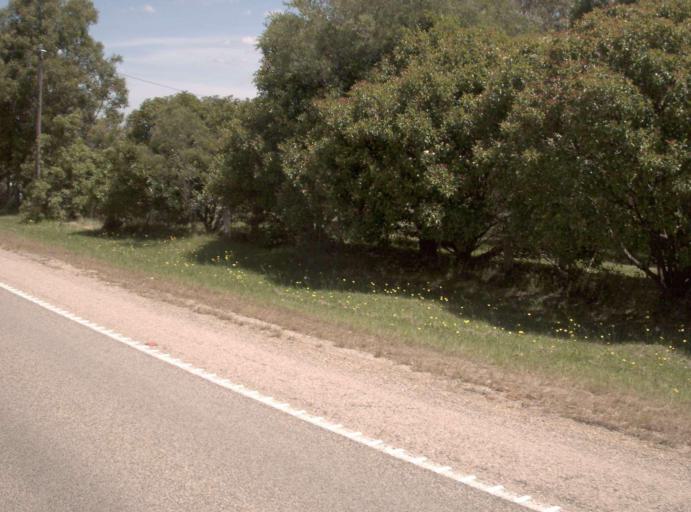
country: AU
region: Victoria
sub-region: East Gippsland
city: Bairnsdale
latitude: -37.7822
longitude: 147.6826
